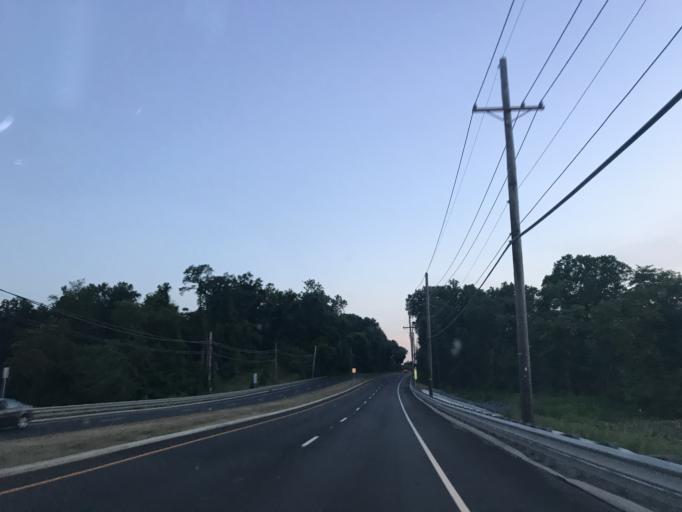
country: US
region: New Jersey
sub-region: Burlington County
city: Bordentown
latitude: 40.1258
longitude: -74.7393
